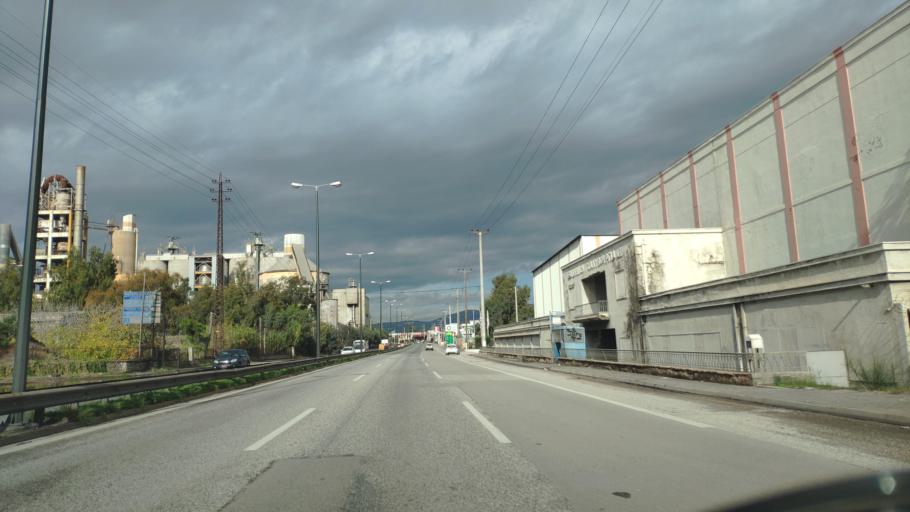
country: GR
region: Attica
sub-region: Nomarchia Athinas
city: Skaramangas
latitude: 38.0330
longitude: 23.5954
